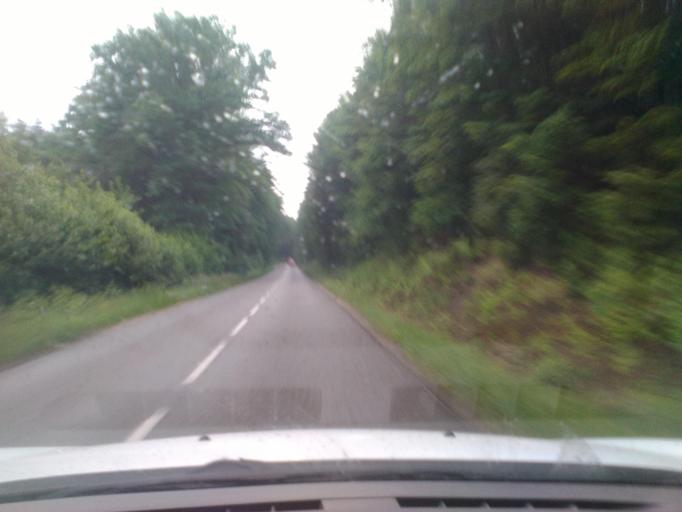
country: FR
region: Lorraine
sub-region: Departement des Vosges
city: Jeanmenil
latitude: 48.2815
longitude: 6.7051
